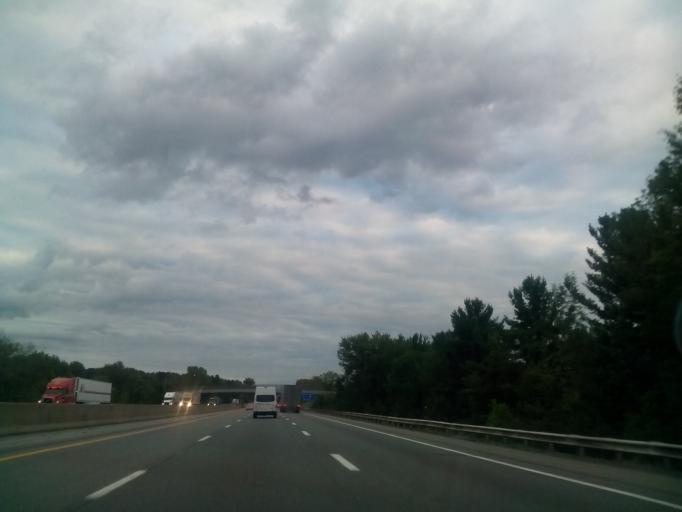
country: US
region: Ohio
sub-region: Trumbull County
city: Newton Falls
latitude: 41.1799
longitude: -80.9255
